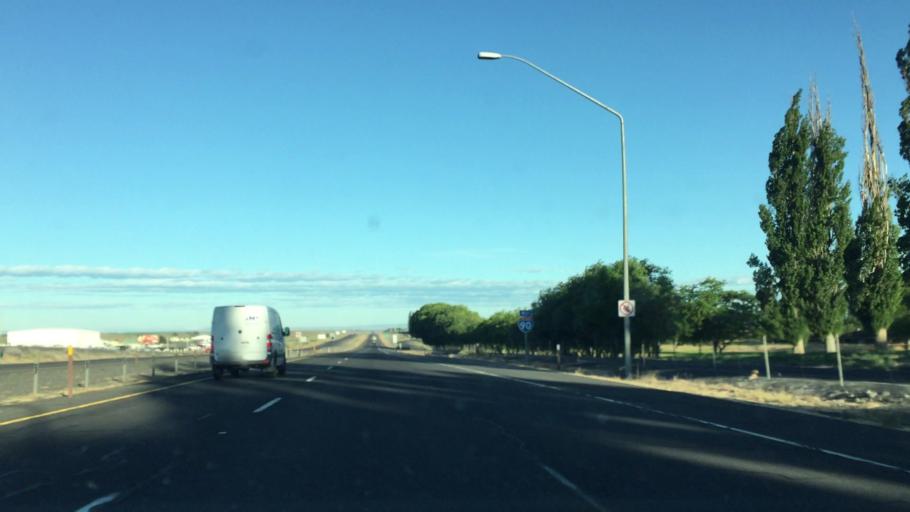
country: US
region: Washington
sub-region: Grant County
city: Cascade Valley
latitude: 47.1046
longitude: -119.3540
